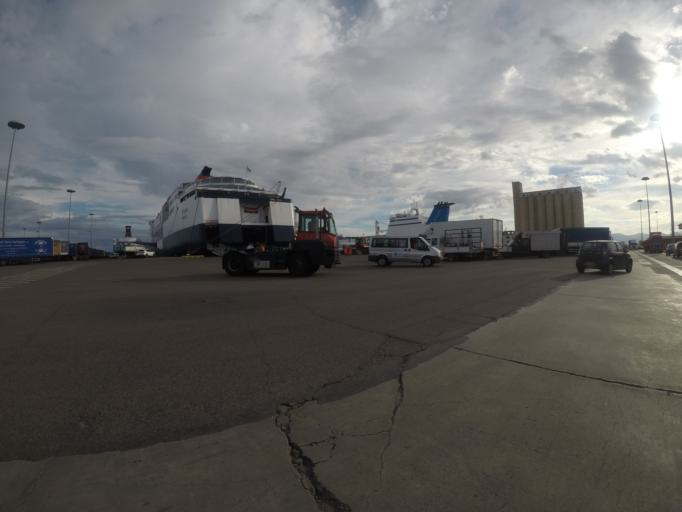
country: IT
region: Sardinia
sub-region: Provincia di Cagliari
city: Cagliari
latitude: 39.2125
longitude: 9.1056
